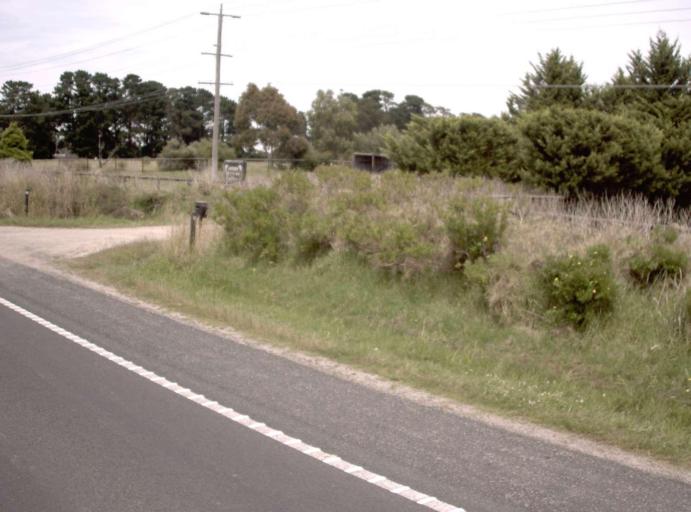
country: AU
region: Victoria
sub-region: Mornington Peninsula
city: Tyabb
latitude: -38.2509
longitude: 145.2150
